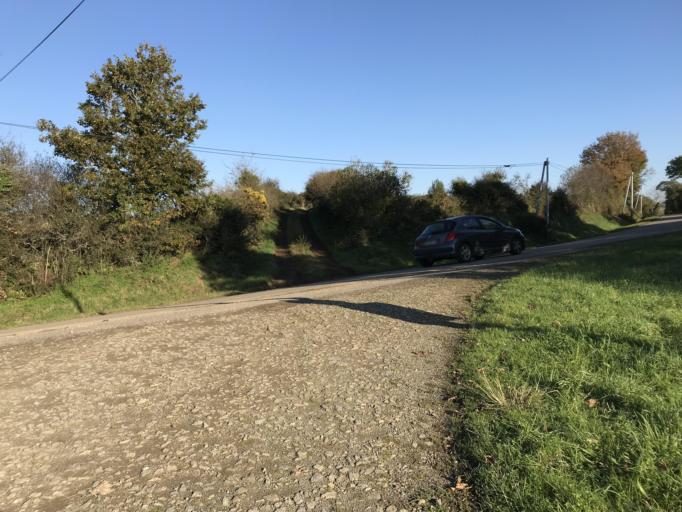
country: FR
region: Brittany
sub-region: Departement du Finistere
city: Hopital-Camfrout
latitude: 48.3149
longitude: -4.2285
